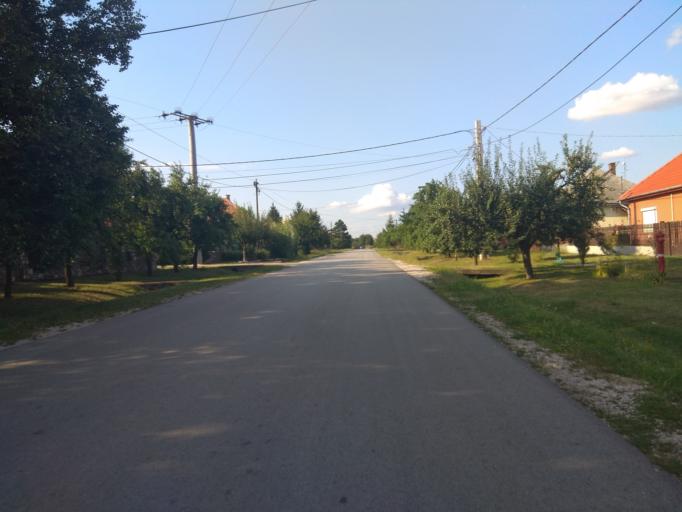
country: HU
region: Borsod-Abauj-Zemplen
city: Emod
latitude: 47.9351
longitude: 20.8080
